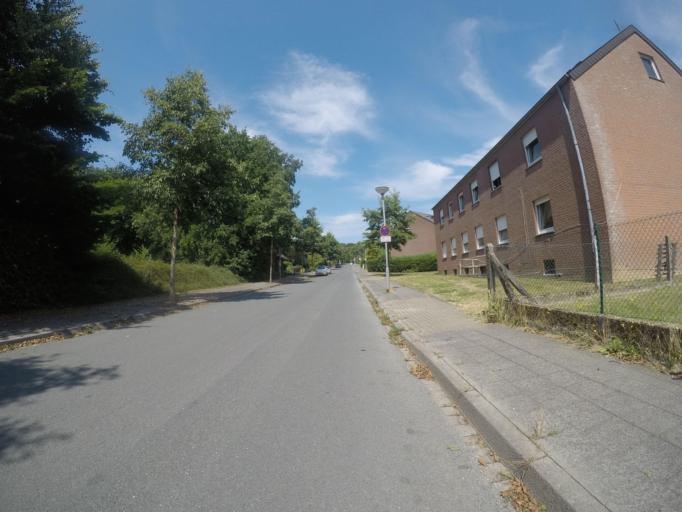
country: DE
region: North Rhine-Westphalia
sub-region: Regierungsbezirk Dusseldorf
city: Kleve
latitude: 51.7798
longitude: 6.1098
